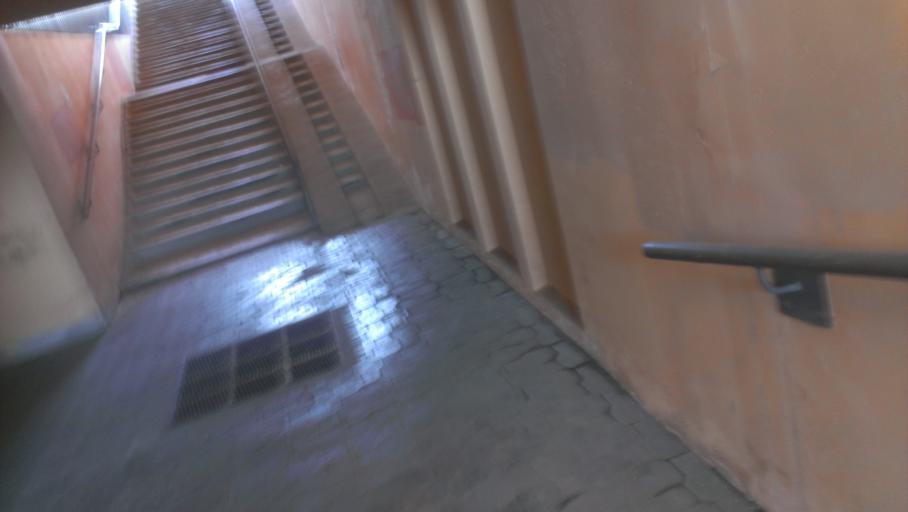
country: RU
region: Altai Krai
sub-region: Gorod Barnaulskiy
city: Barnaul
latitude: 53.3412
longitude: 83.7038
